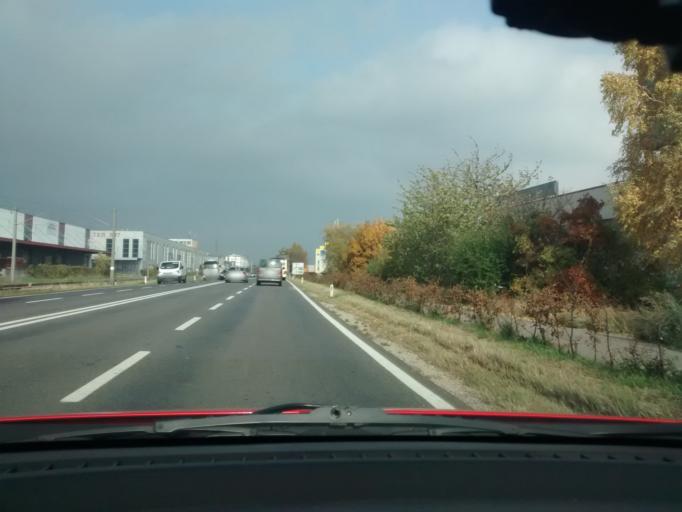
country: AT
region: Lower Austria
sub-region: Politischer Bezirk Modling
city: Wiener Neudorf
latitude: 48.0736
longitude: 16.3118
